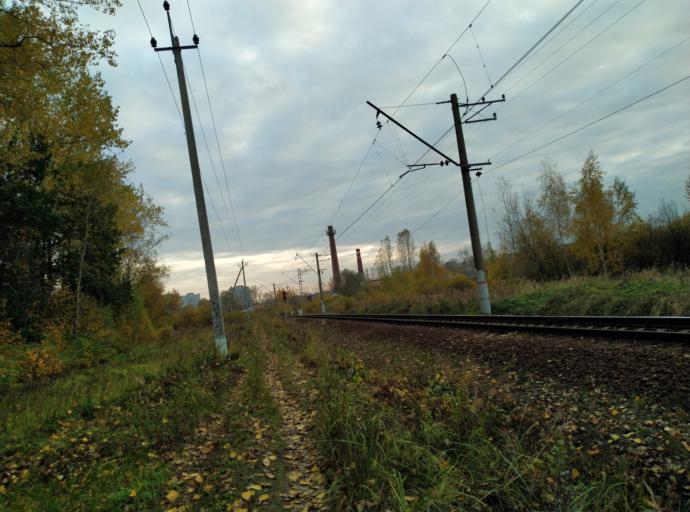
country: RU
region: Moskovskaya
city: Bol'shiye Vyazemy
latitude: 55.6187
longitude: 36.9729
